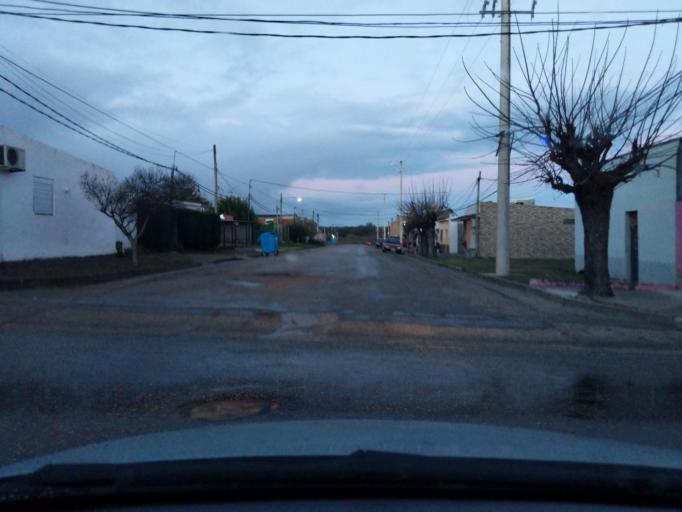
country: UY
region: Florida
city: Florida
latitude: -34.1083
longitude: -56.2089
